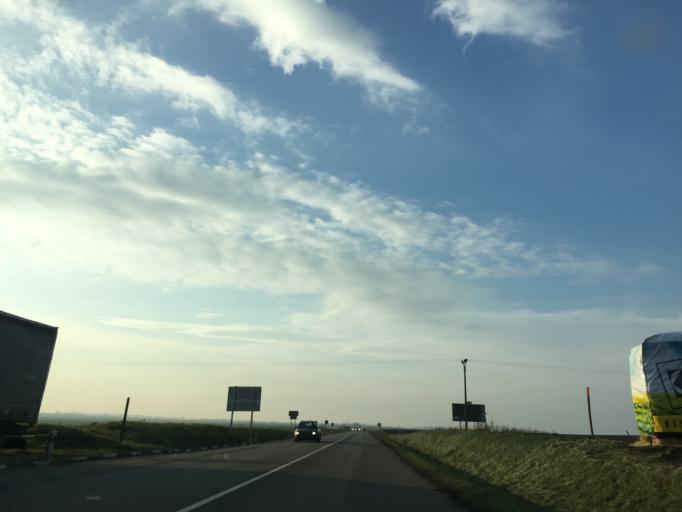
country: SK
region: Nitriansky
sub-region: Okres Komarno
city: Hurbanovo
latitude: 47.9118
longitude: 18.3048
